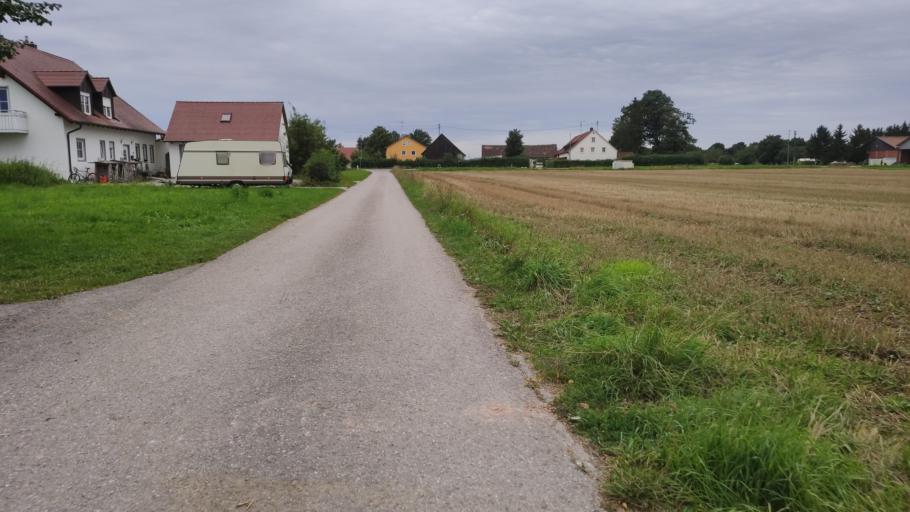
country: DE
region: Bavaria
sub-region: Swabia
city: Oberottmarshausen
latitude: 48.2432
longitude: 10.8776
